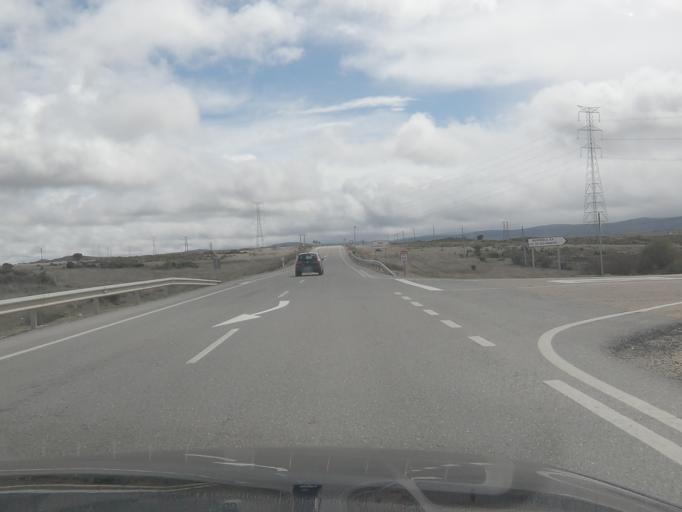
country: ES
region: Castille and Leon
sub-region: Provincia de Zamora
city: Villardeciervos
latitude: 42.0004
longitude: -6.2503
